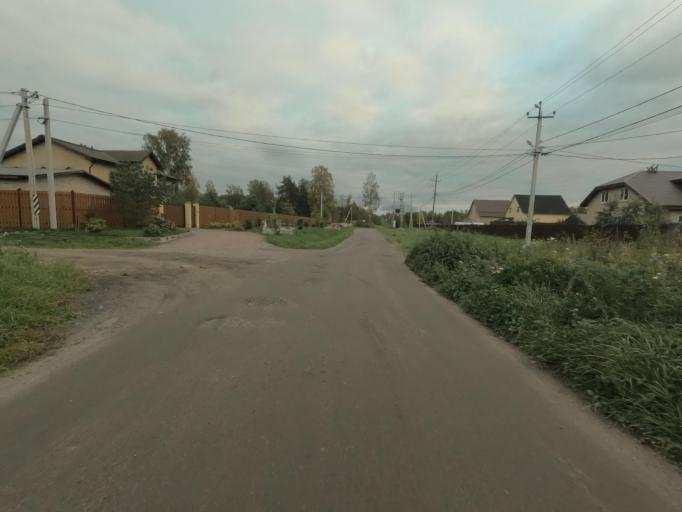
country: RU
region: Leningrad
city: Pavlovo
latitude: 59.8108
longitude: 30.9185
